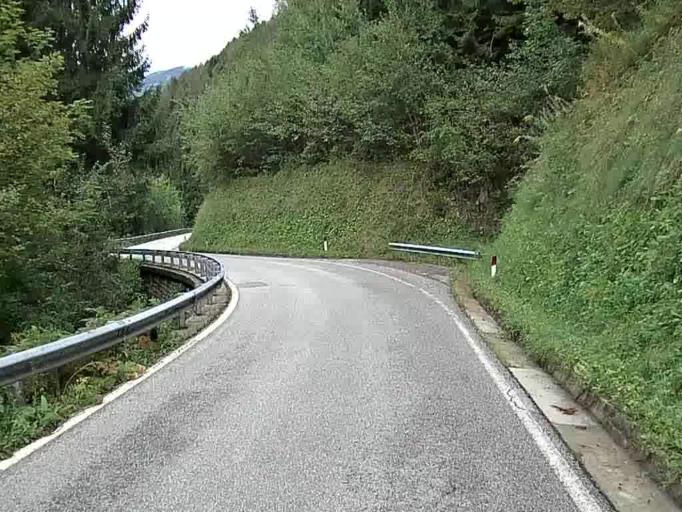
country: IT
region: Trentino-Alto Adige
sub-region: Provincia di Trento
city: Frassilongo
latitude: 46.0772
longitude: 11.2894
